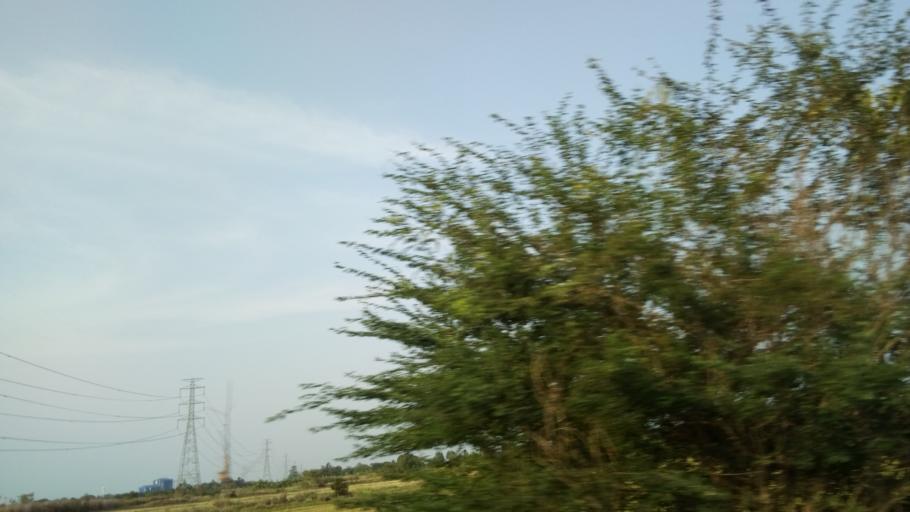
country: TH
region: Sara Buri
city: Nong Khae
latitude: 14.2798
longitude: 100.8183
